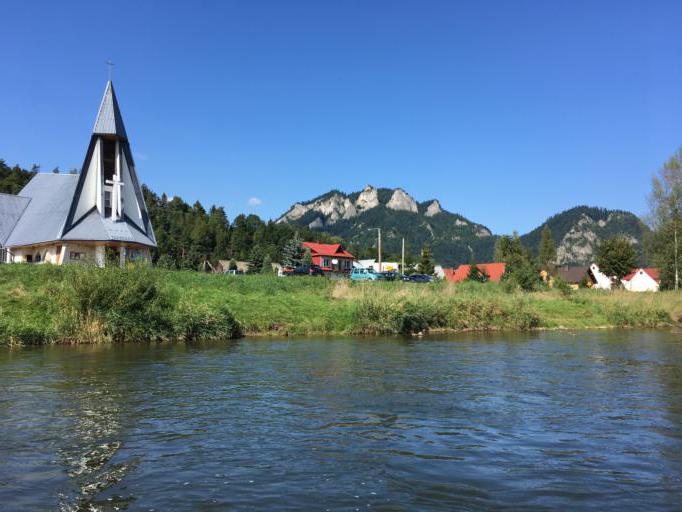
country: PL
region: Lesser Poland Voivodeship
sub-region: Powiat nowotarski
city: Kroscienko nad Dunajcem
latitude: 49.3926
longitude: 20.4048
